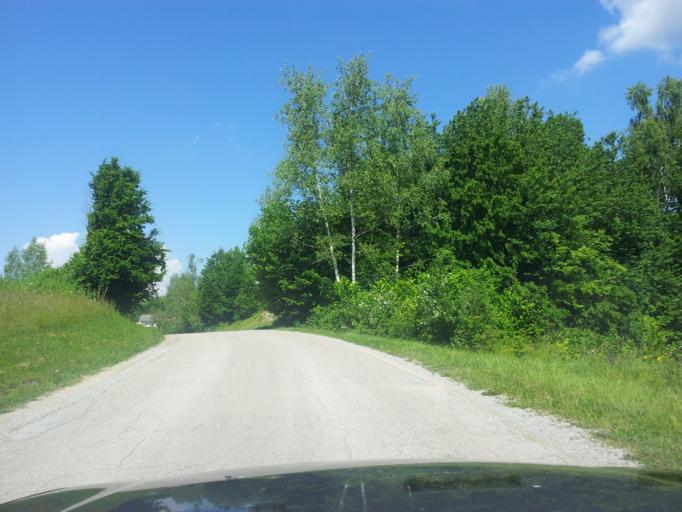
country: HR
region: Karlovacka
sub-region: Grad Karlovac
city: Karlovac
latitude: 45.4740
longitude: 15.4644
